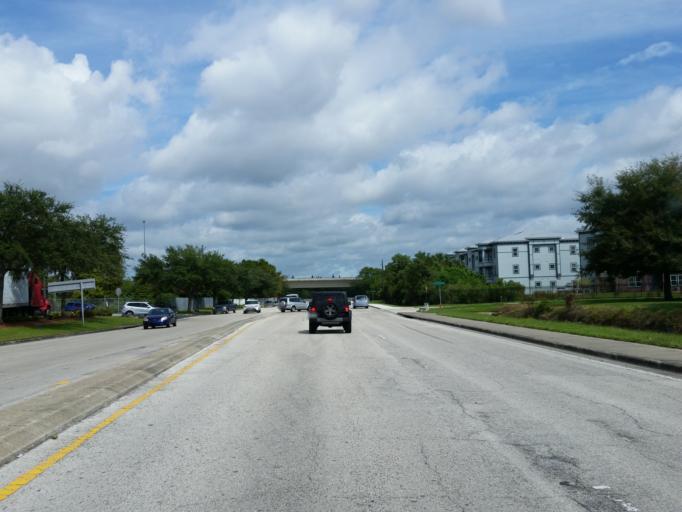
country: US
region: Florida
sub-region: Hillsborough County
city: Brandon
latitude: 27.9242
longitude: -82.3228
